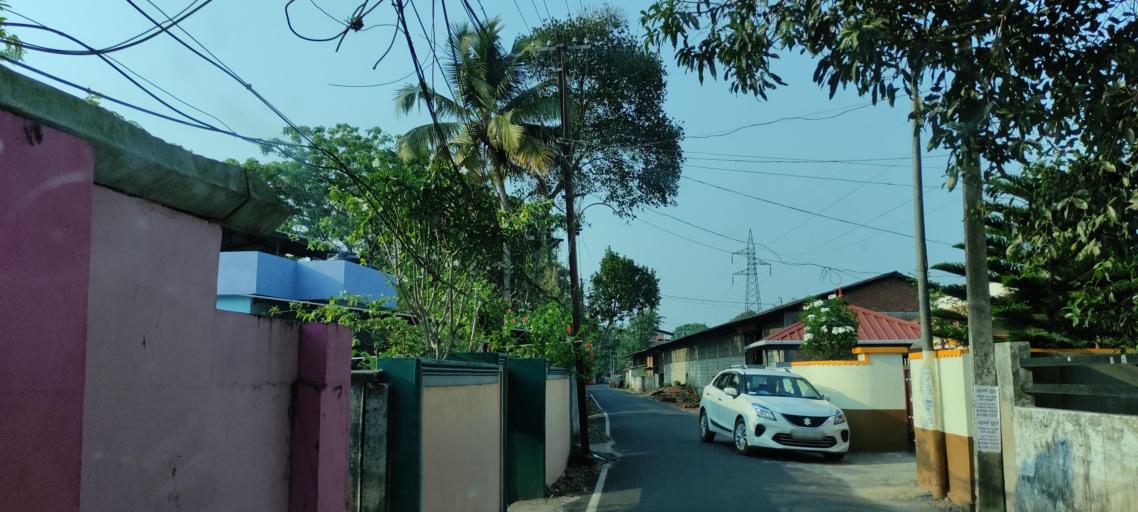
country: IN
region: Kerala
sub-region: Alappuzha
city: Alleppey
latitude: 9.5147
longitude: 76.3224
